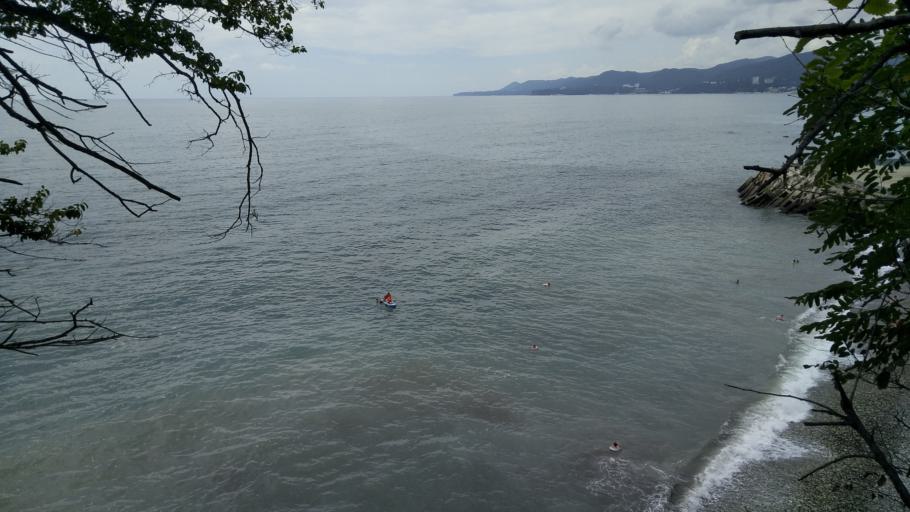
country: RU
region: Krasnodarskiy
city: Agoy
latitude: 44.1331
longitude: 39.0261
